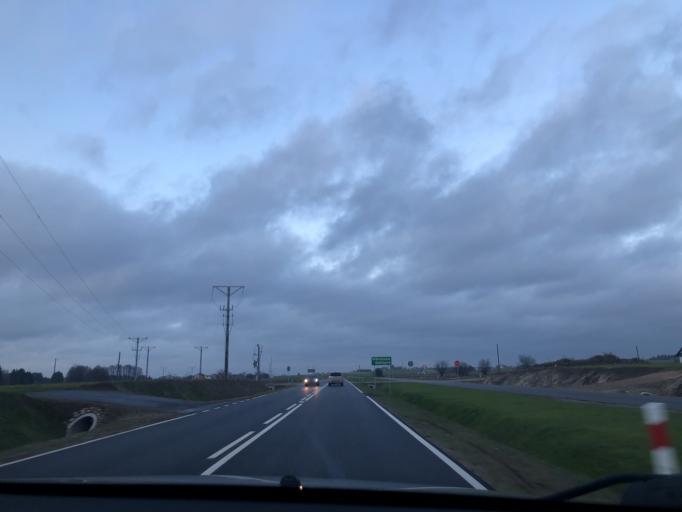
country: PL
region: Podlasie
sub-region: Lomza
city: Lomza
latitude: 53.1361
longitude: 22.0504
